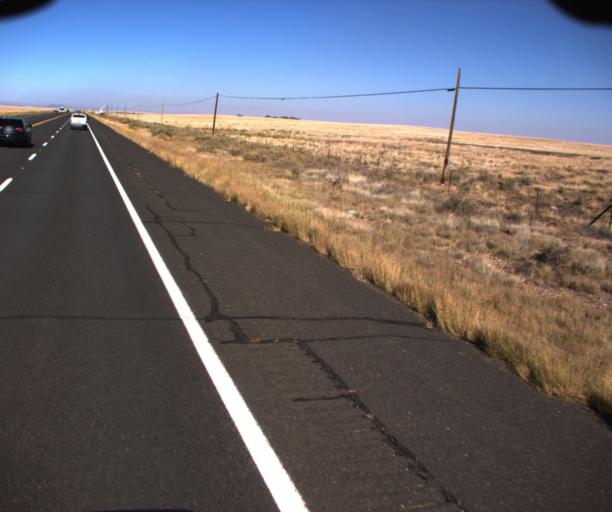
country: US
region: Arizona
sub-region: Coconino County
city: Flagstaff
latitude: 35.6258
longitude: -111.5209
